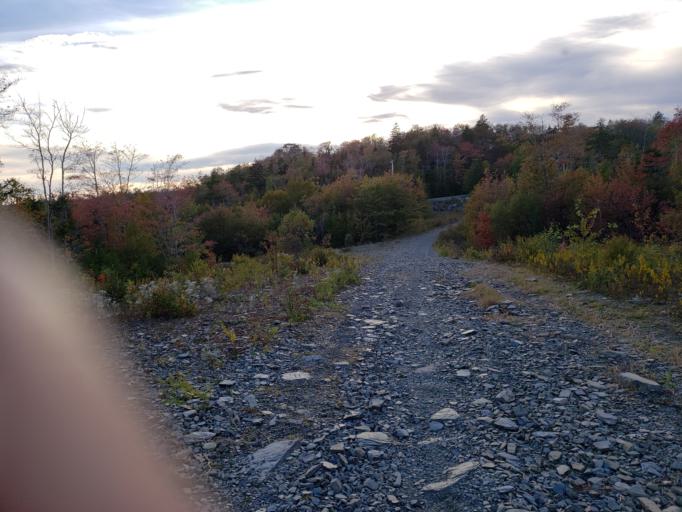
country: CA
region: Nova Scotia
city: Cole Harbour
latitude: 44.7436
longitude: -63.3771
